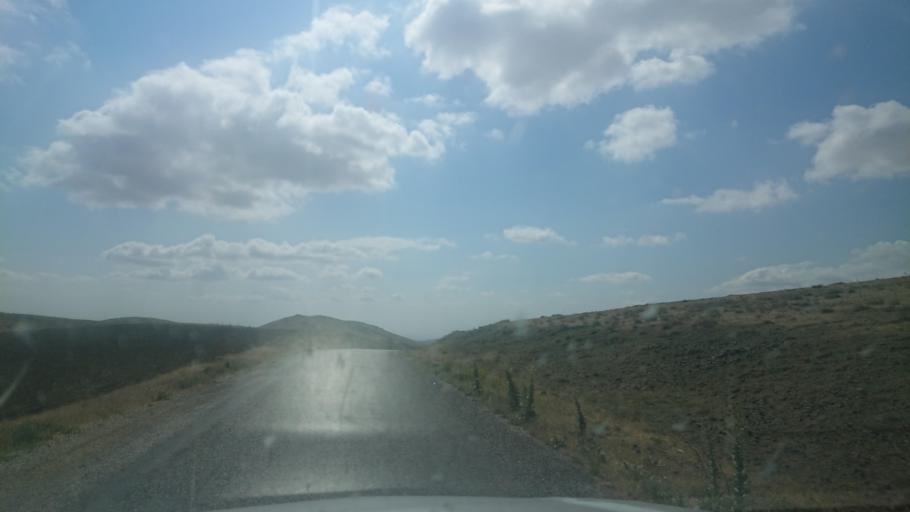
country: TR
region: Aksaray
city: Sariyahsi
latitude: 39.0020
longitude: 33.9717
